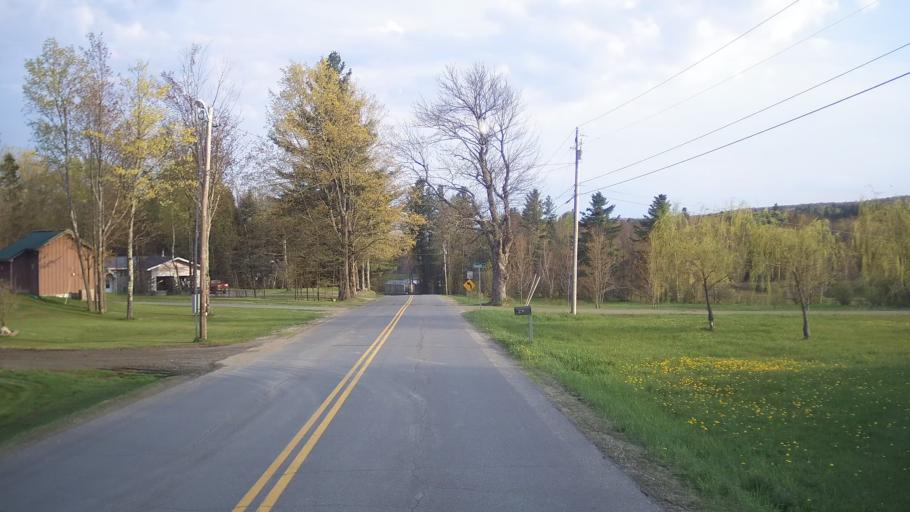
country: US
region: Vermont
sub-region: Orleans County
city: Newport
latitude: 44.8960
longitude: -72.4313
